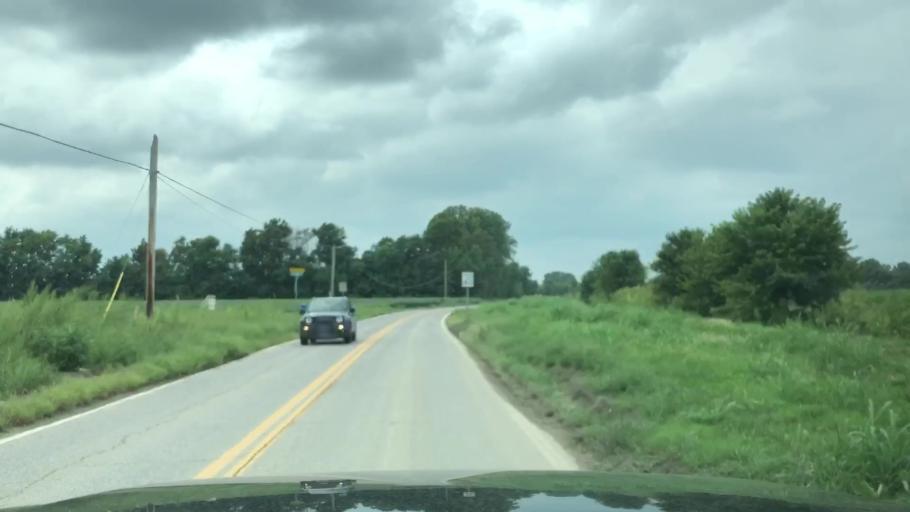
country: US
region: Missouri
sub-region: Saint Louis County
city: Bridgeton
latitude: 38.7989
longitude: -90.4141
